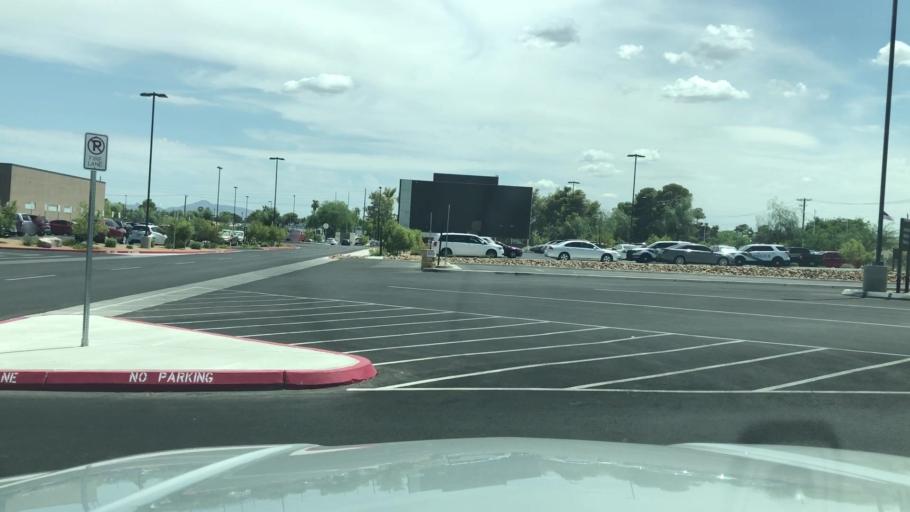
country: US
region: Nevada
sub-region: Clark County
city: Winchester
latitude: 36.1467
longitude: -115.1138
